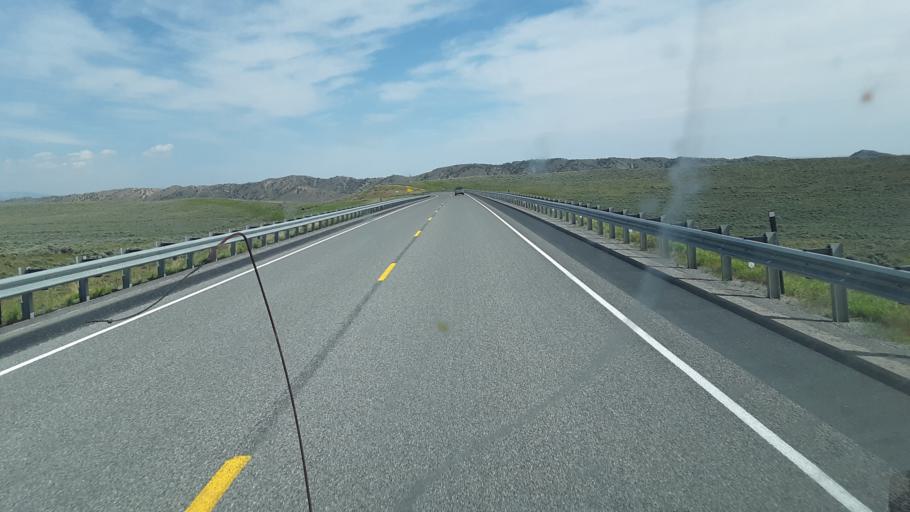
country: US
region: Wyoming
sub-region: Park County
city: Cody
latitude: 44.2663
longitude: -108.8723
